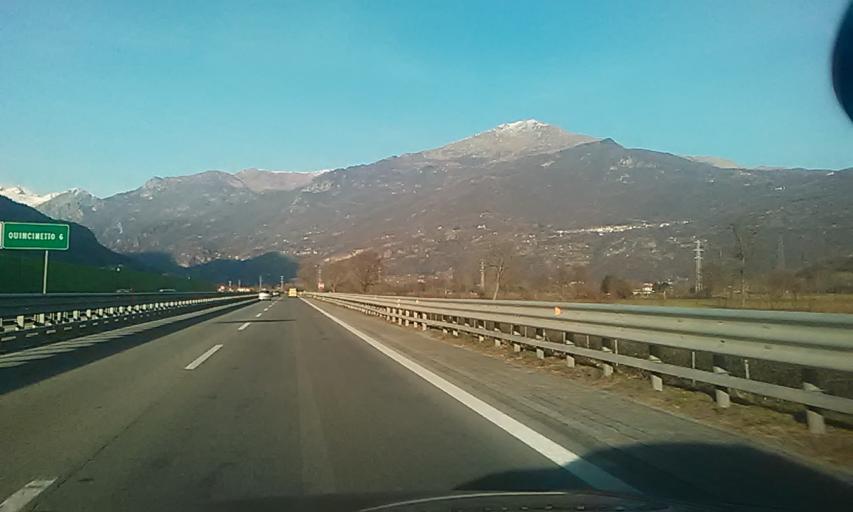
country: IT
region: Piedmont
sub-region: Provincia di Torino
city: Quassolo
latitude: 45.5087
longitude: 7.8327
